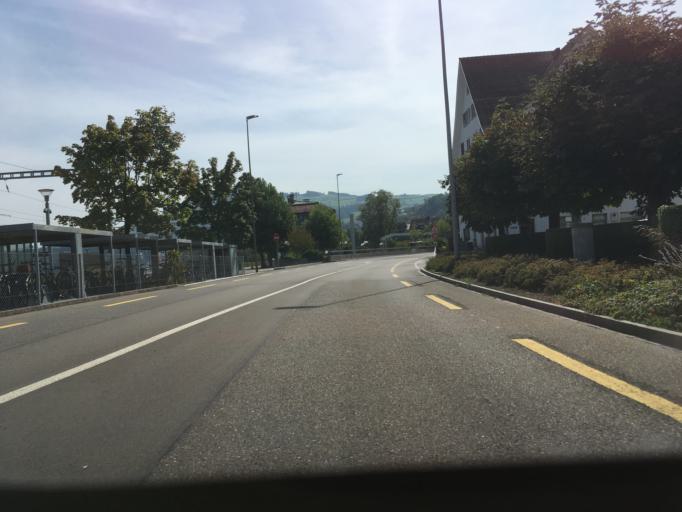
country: CH
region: Zurich
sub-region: Bezirk Horgen
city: Richterswil / Dorfkern
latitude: 47.2092
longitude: 8.7063
